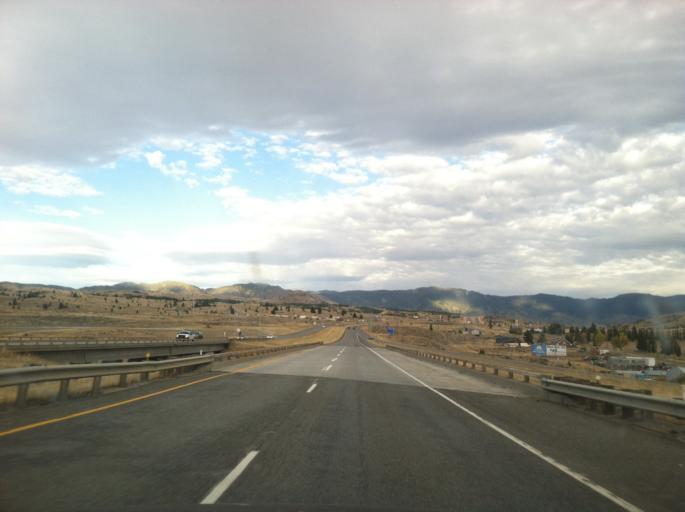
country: US
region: Montana
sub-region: Silver Bow County
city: Butte
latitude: 46.0079
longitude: -112.6396
